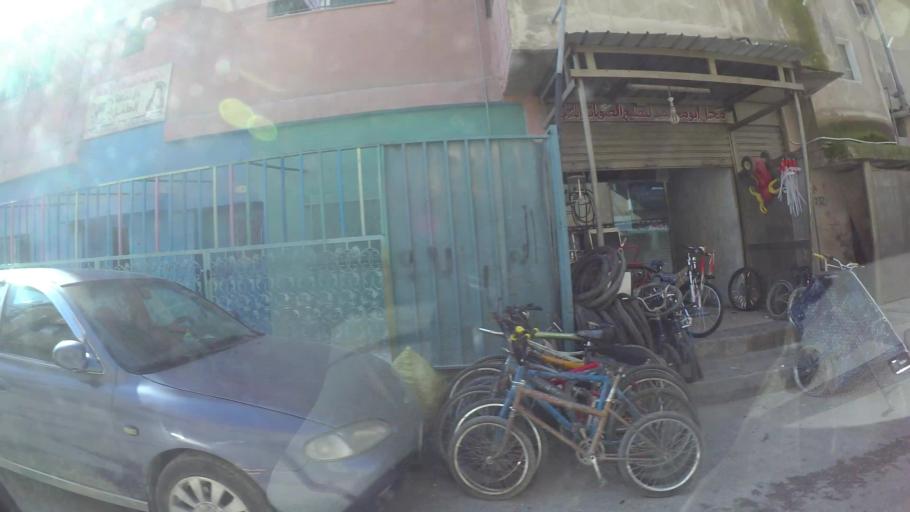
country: JO
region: Amman
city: Al Jubayhah
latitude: 32.0757
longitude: 35.8402
